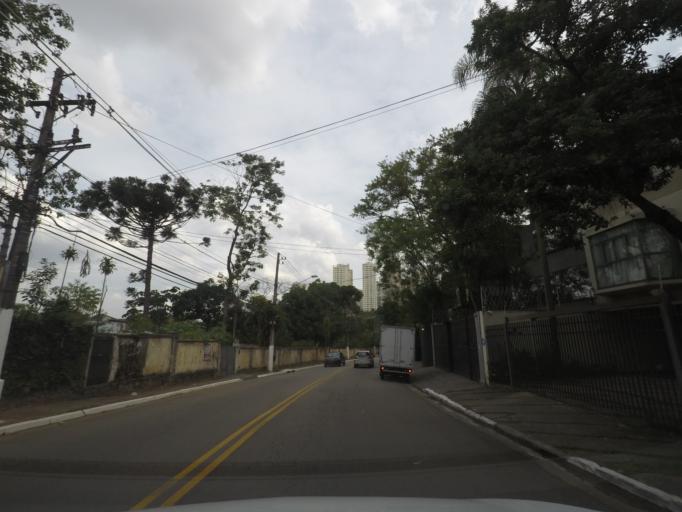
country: BR
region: Sao Paulo
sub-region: Taboao Da Serra
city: Taboao da Serra
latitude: -23.6238
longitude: -46.7165
